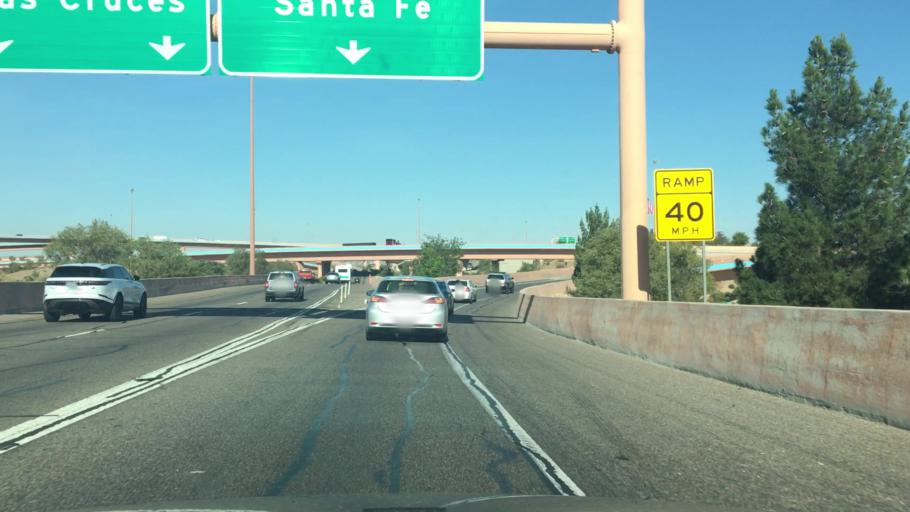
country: US
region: New Mexico
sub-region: Bernalillo County
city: Albuquerque
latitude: 35.1066
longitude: -106.6251
